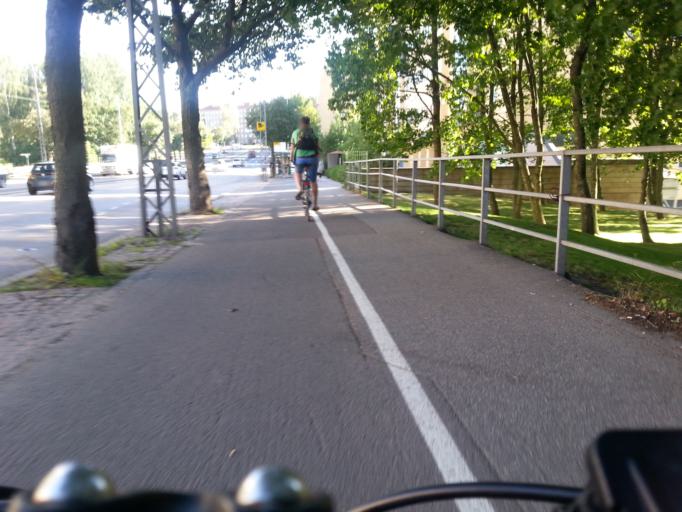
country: FI
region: Uusimaa
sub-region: Helsinki
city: Helsinki
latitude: 60.1983
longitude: 24.9010
